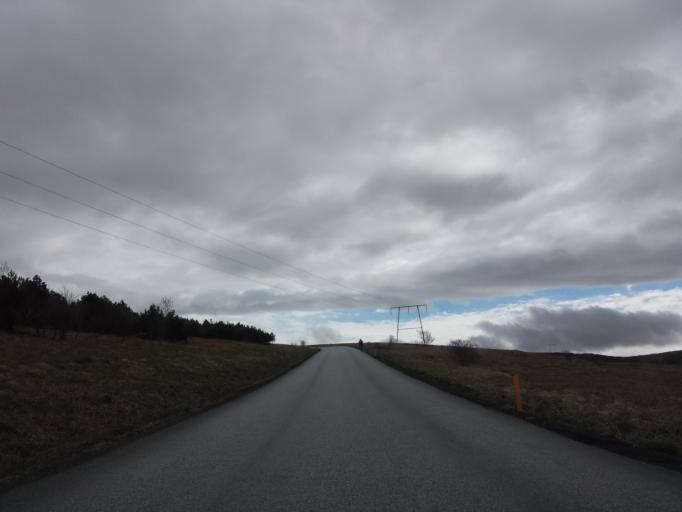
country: IS
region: Capital Region
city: Kopavogur
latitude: 64.0810
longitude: -21.8644
